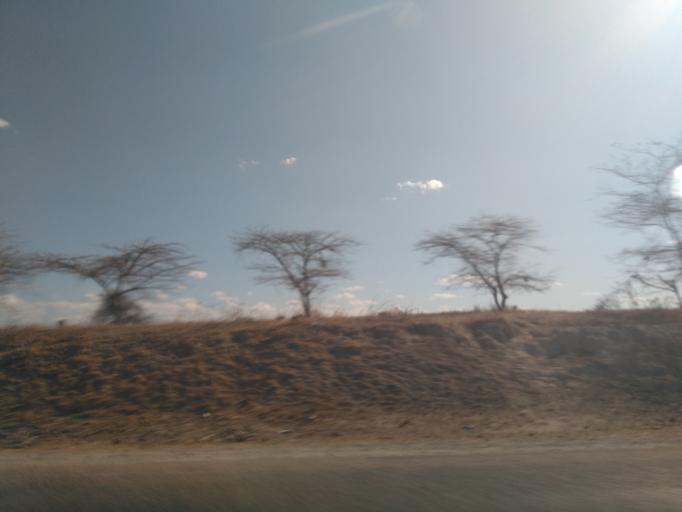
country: TZ
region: Dodoma
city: Dodoma
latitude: -6.1516
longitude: 35.7068
